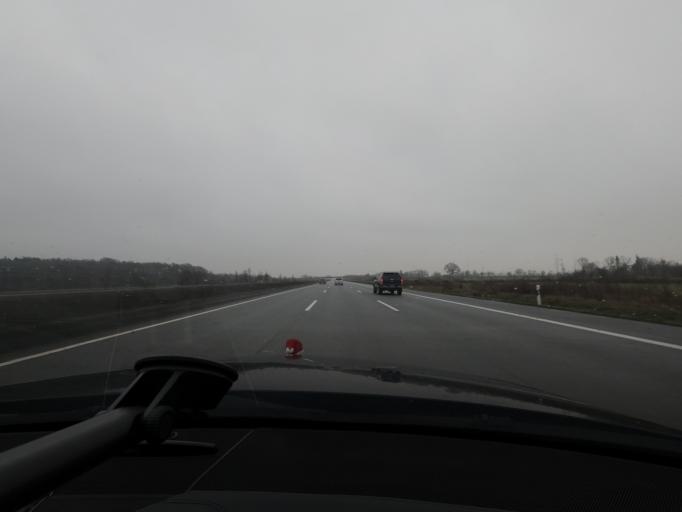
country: DE
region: Schleswig-Holstein
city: Grossenaspe
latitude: 53.9882
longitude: 9.9404
